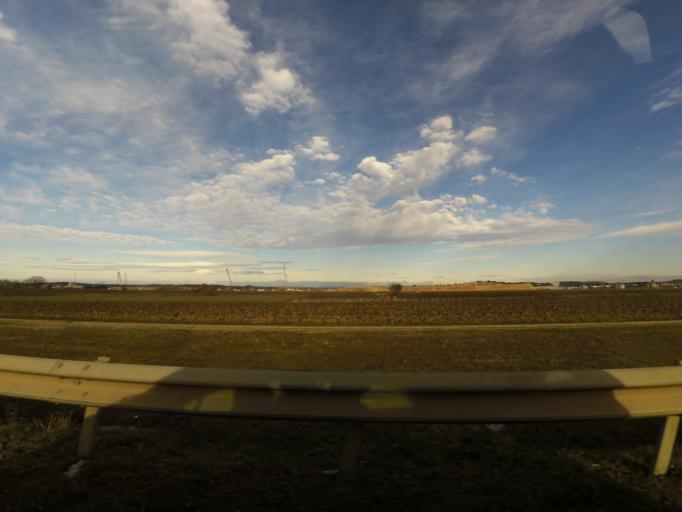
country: FR
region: Languedoc-Roussillon
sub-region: Departement du Gard
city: Gallargues-le-Montueux
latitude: 43.7008
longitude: 4.1813
